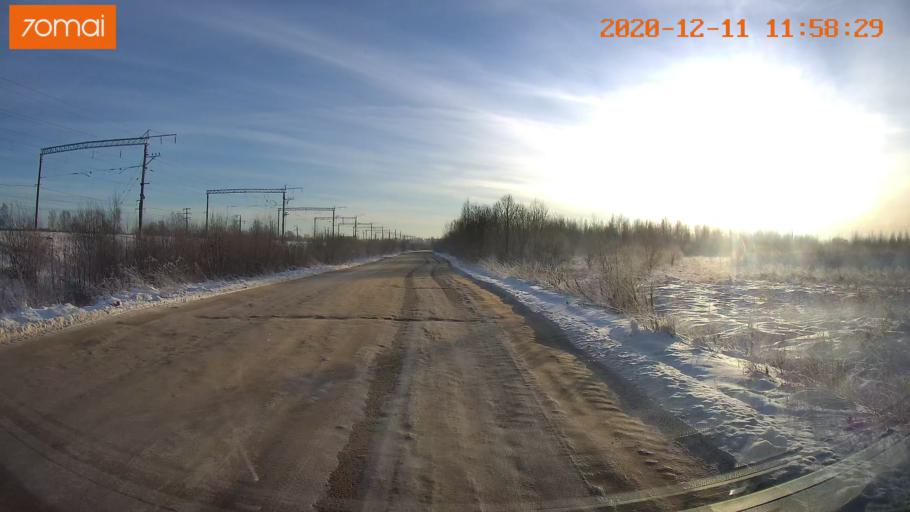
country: RU
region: Kostroma
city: Buy
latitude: 58.4838
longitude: 41.5087
